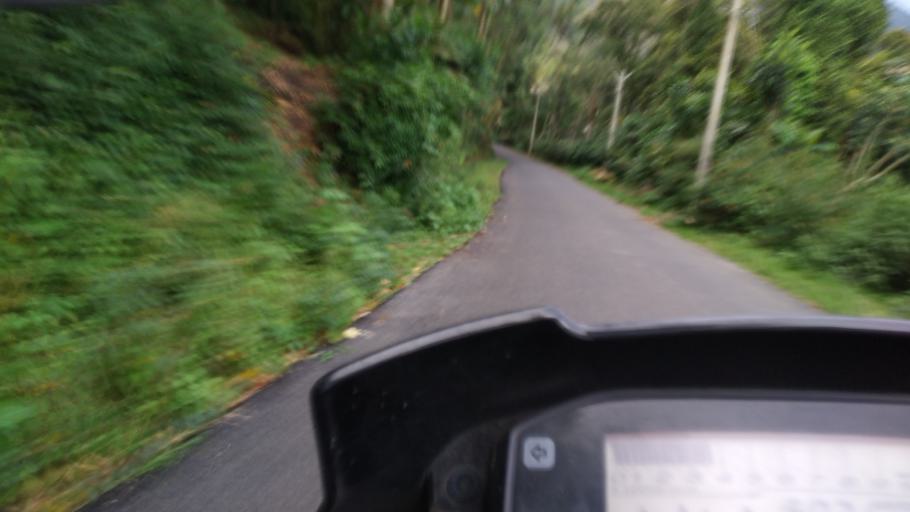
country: IN
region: Tamil Nadu
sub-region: Theni
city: Bodinayakkanur
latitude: 10.0334
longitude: 77.2274
